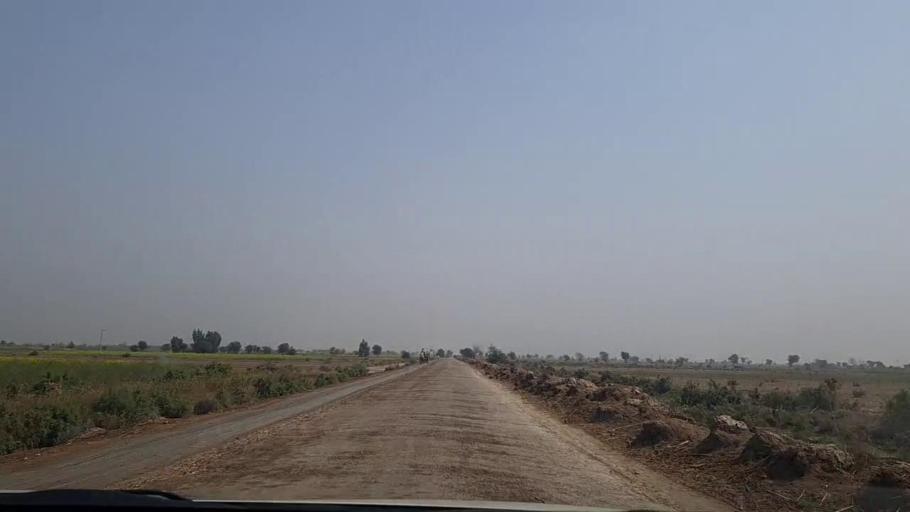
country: PK
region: Sindh
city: Pithoro
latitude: 25.5570
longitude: 69.2007
